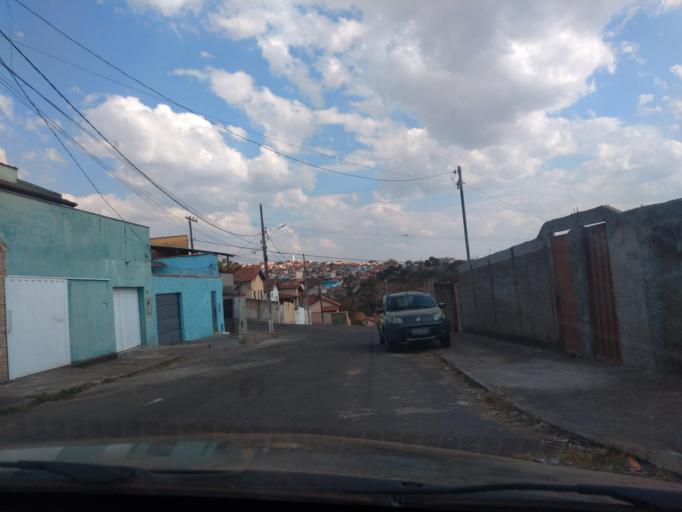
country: BR
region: Minas Gerais
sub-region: Tres Coracoes
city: Tres Coracoes
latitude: -21.6830
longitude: -45.2371
